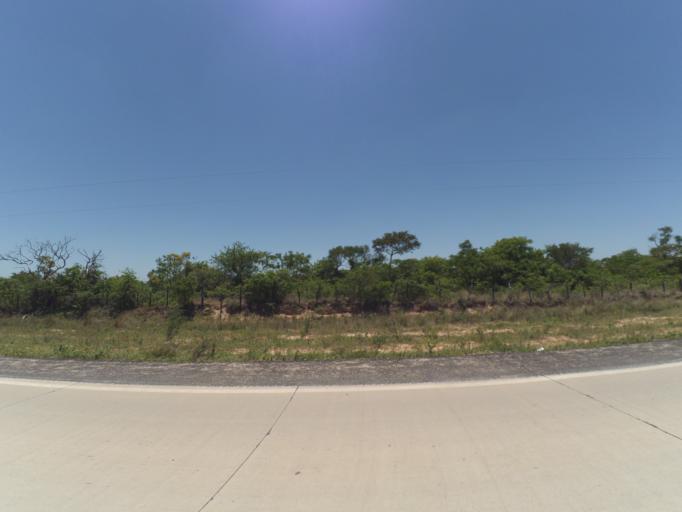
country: BO
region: Santa Cruz
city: Santa Cruz de la Sierra
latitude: -17.8144
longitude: -63.2839
